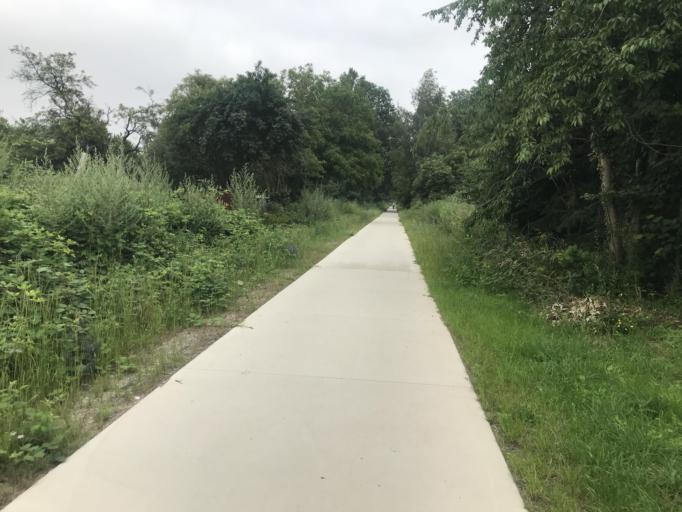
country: DE
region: Saxony-Anhalt
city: Ballenstedt
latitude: 51.7232
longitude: 11.2313
